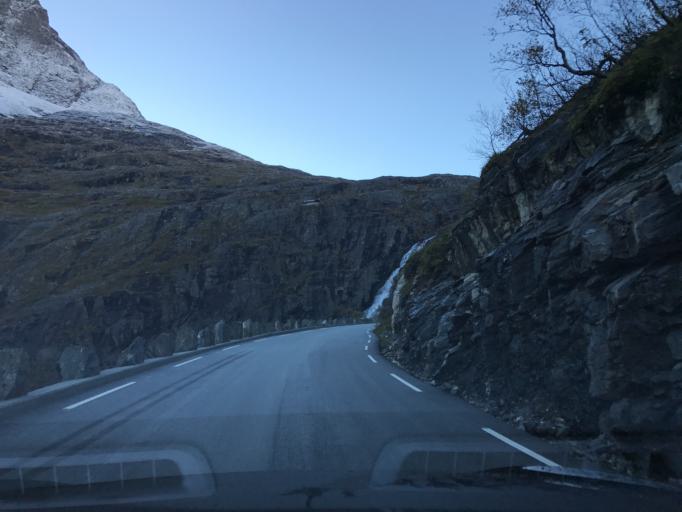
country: NO
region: More og Romsdal
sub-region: Rauma
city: Andalsnes
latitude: 62.4597
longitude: 7.6702
